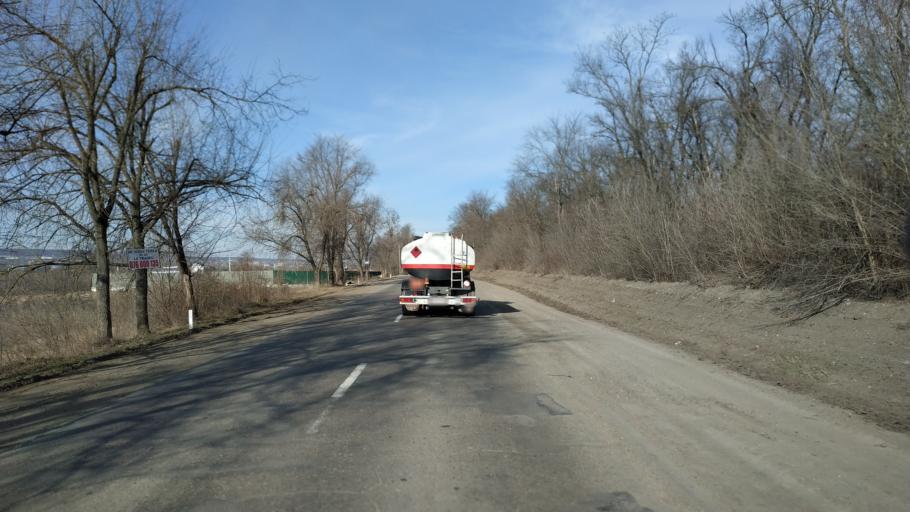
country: MD
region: Laloveni
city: Ialoveni
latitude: 46.9540
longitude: 28.7570
